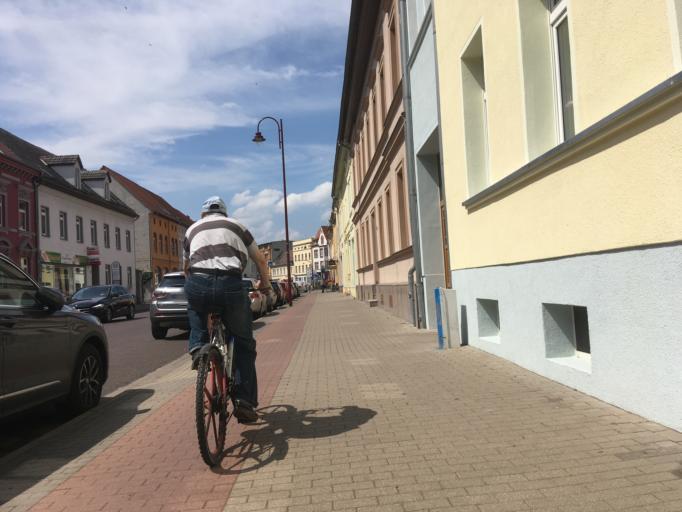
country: DE
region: Saxony-Anhalt
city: Koethen
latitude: 51.7526
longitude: 11.9845
